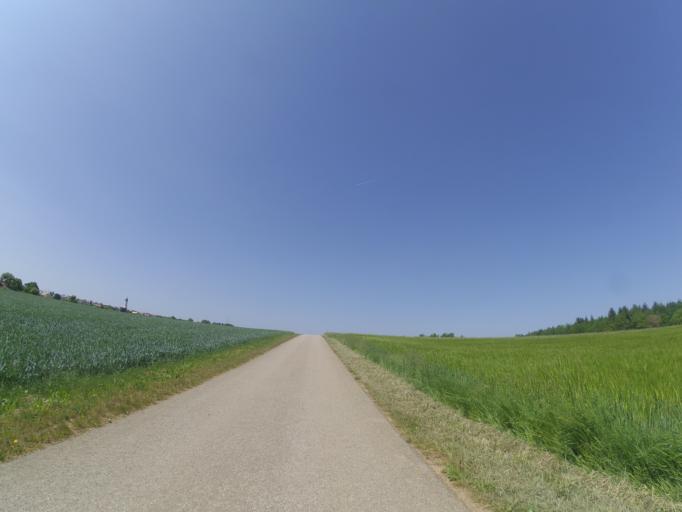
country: DE
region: Baden-Wuerttemberg
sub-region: Tuebingen Region
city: Merklingen
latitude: 48.5045
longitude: 9.7665
